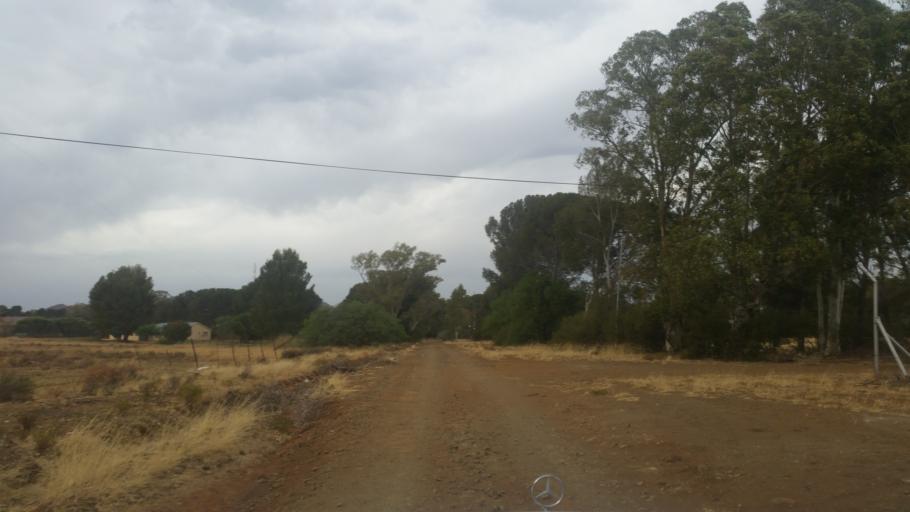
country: ZA
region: Orange Free State
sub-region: Xhariep District Municipality
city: Trompsburg
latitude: -30.4975
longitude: 25.9652
